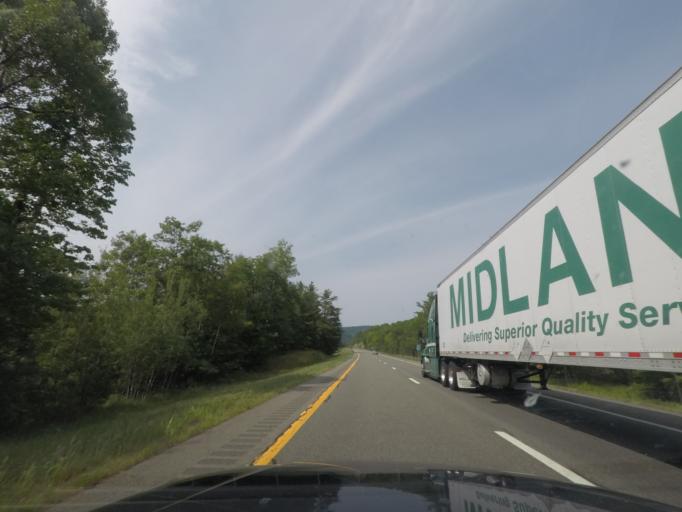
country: US
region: New York
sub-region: Essex County
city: Keeseville
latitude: 44.3592
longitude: -73.5309
